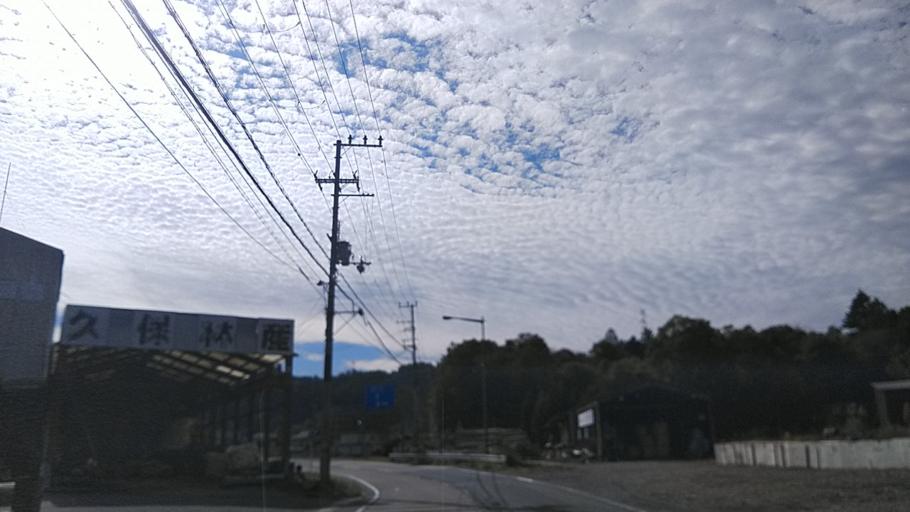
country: JP
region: Kyoto
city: Kameoka
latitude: 35.1741
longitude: 135.6312
